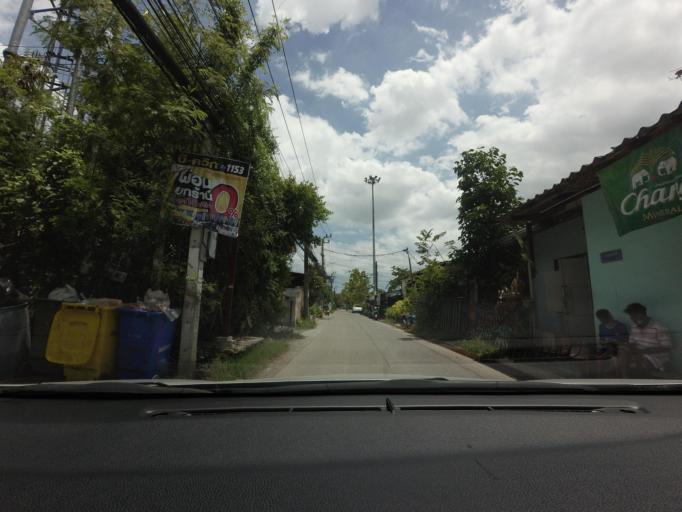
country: TH
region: Samut Prakan
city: Phra Samut Chedi
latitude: 13.6242
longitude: 100.5822
